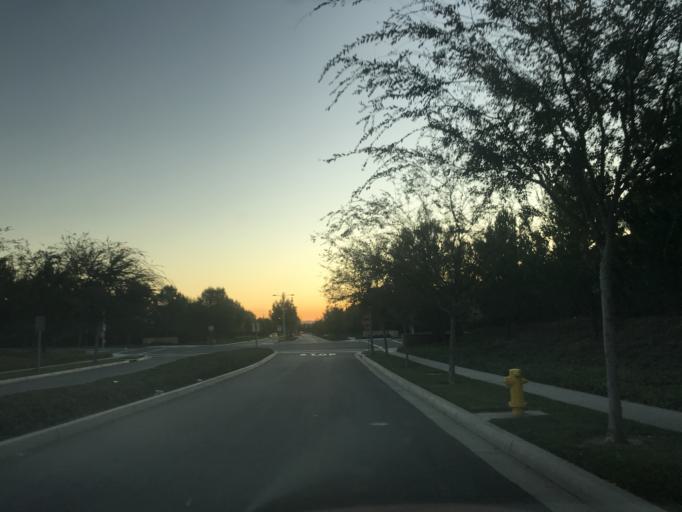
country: US
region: California
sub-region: Orange County
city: North Tustin
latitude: 33.7107
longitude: -117.7417
